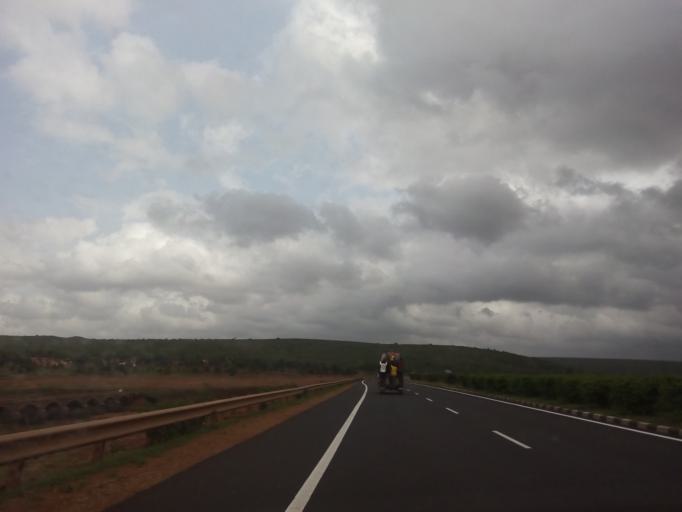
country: IN
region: Karnataka
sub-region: Belgaum
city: Hukeri
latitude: 16.0730
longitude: 74.5183
